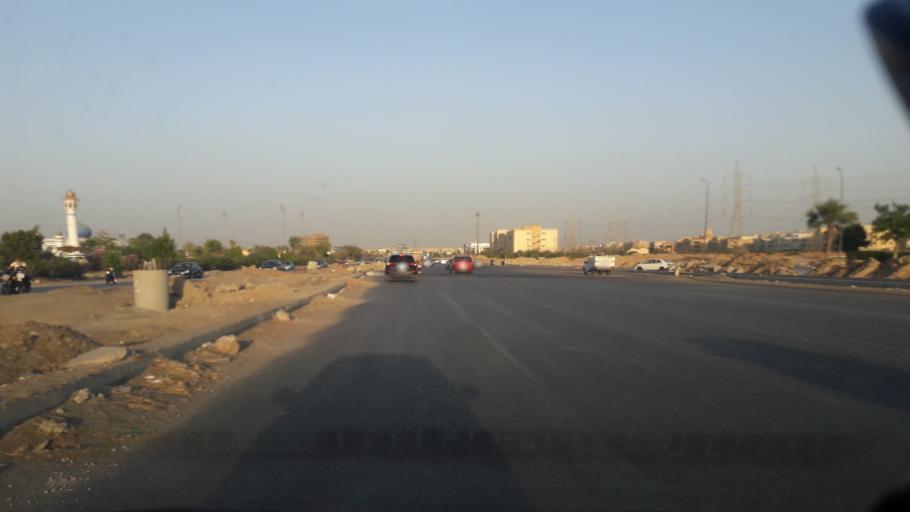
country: EG
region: Al Jizah
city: Madinat Sittah Uktubar
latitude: 29.9609
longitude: 31.0469
